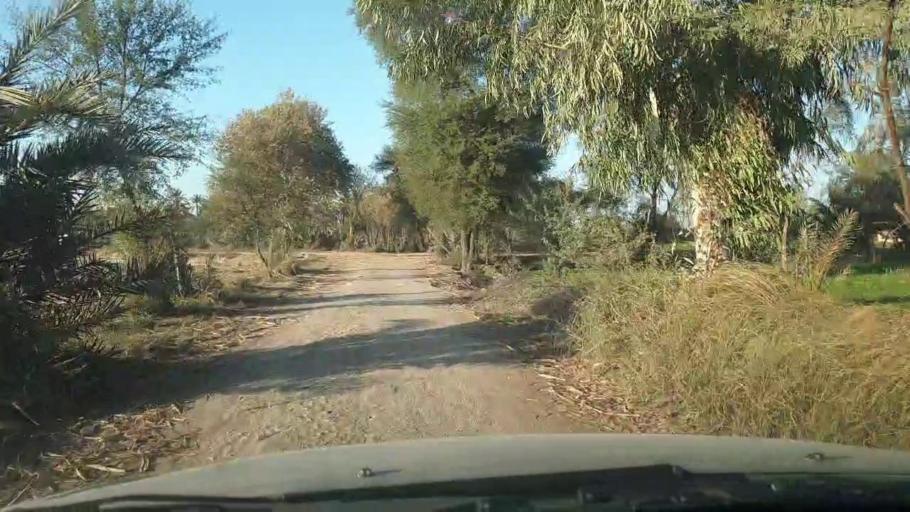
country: PK
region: Sindh
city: Ghotki
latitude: 28.0265
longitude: 69.3080
